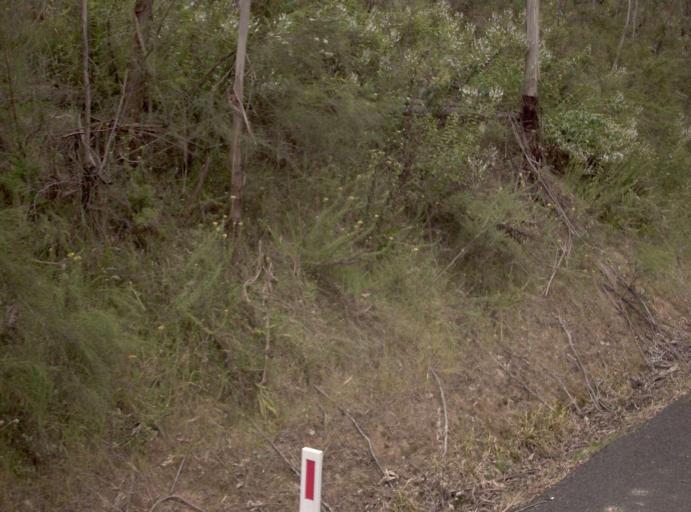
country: AU
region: New South Wales
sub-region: Bombala
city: Bombala
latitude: -37.3670
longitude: 149.1971
